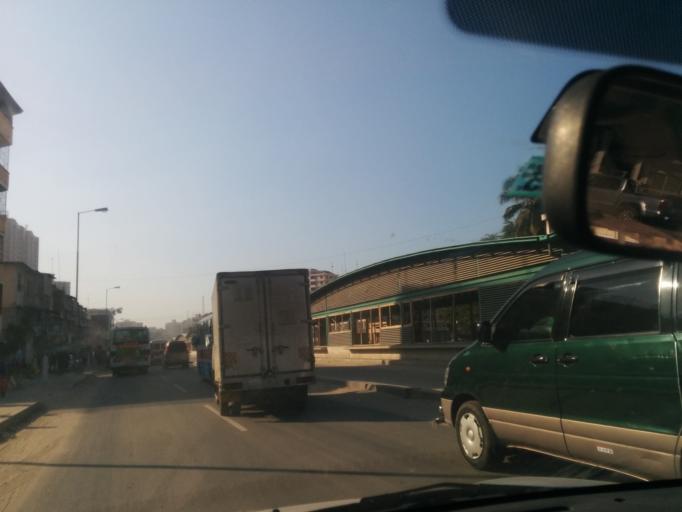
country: TZ
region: Dar es Salaam
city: Dar es Salaam
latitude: -6.8130
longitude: 39.2737
